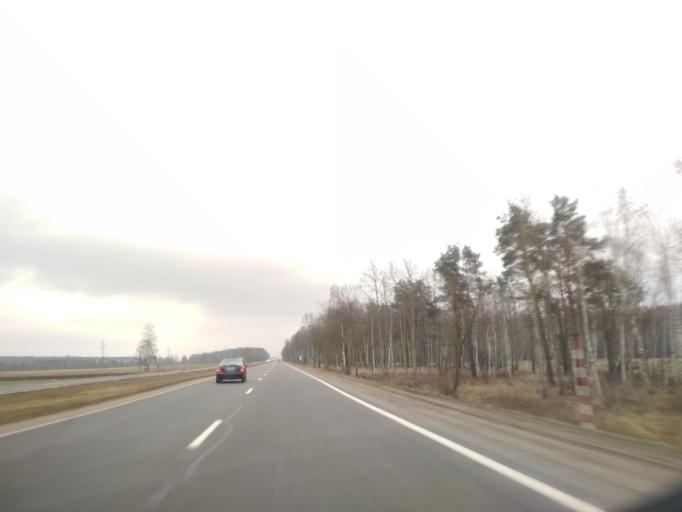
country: BY
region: Minsk
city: Dukora
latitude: 53.6298
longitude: 28.0248
